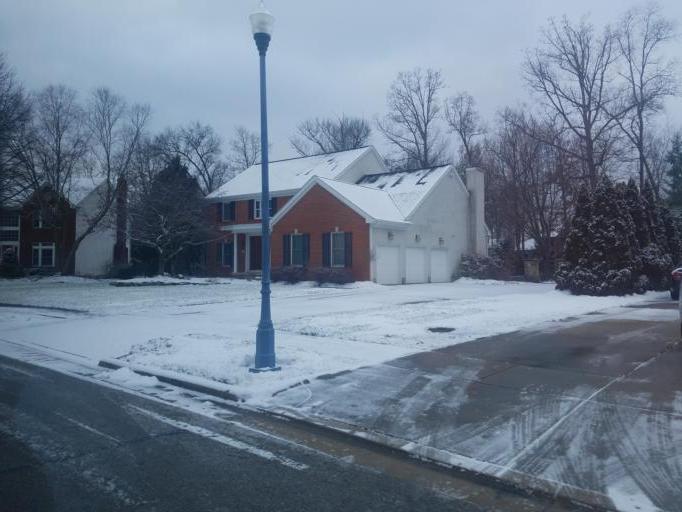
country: US
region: Ohio
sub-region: Franklin County
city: New Albany
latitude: 40.0526
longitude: -82.8332
